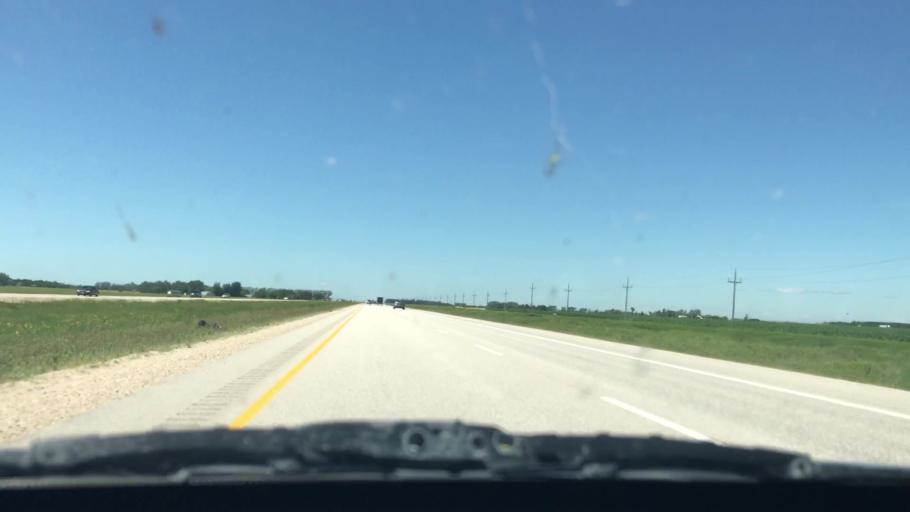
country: CA
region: Manitoba
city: Steinbach
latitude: 49.7262
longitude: -96.7086
